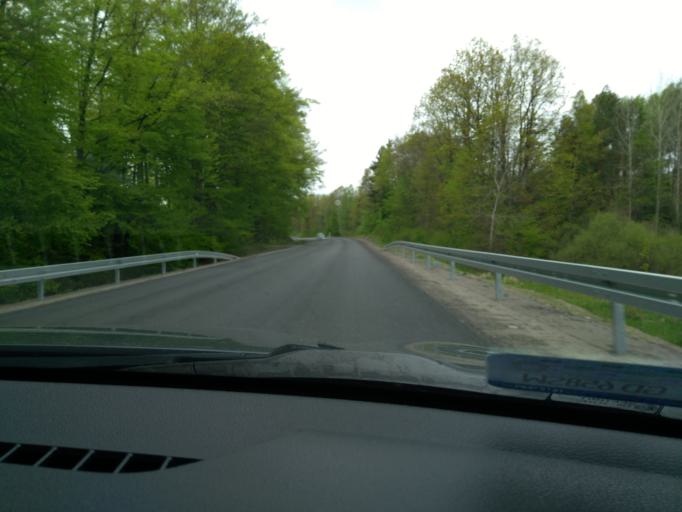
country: PL
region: Pomeranian Voivodeship
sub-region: Powiat kartuski
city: Kartuzy
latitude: 54.3422
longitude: 18.1778
